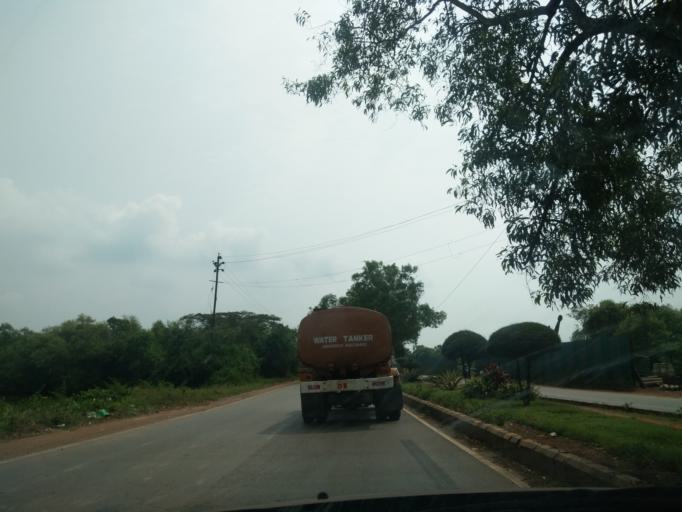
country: IN
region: Goa
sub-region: North Goa
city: Panaji
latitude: 15.4930
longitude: 73.8416
